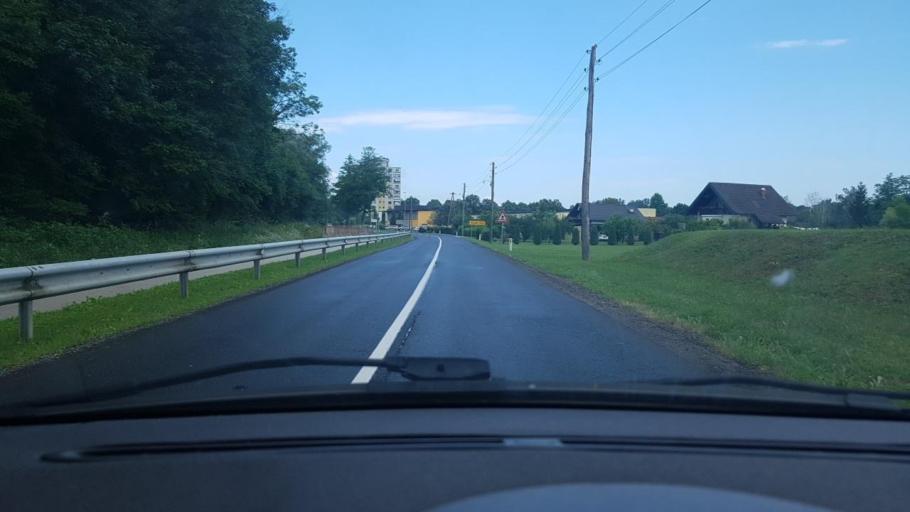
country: AT
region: Styria
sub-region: Politischer Bezirk Suedoststeiermark
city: Mureck
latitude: 46.6972
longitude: 15.7446
